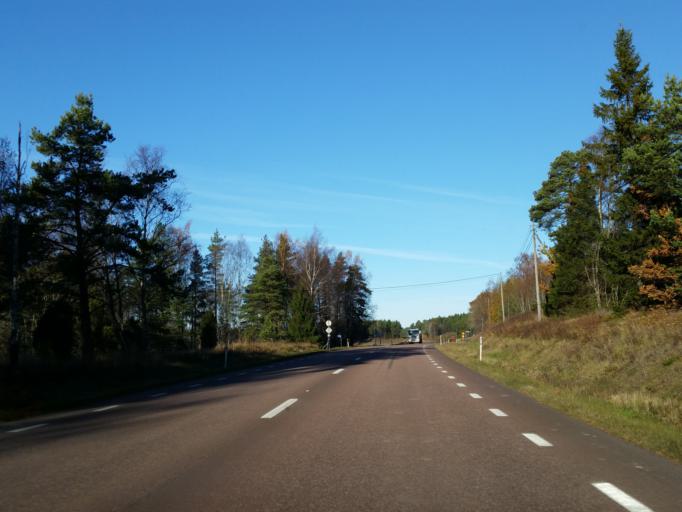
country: AX
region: Alands landsbygd
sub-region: Finstroem
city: Finstroem
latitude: 60.2524
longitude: 19.9634
